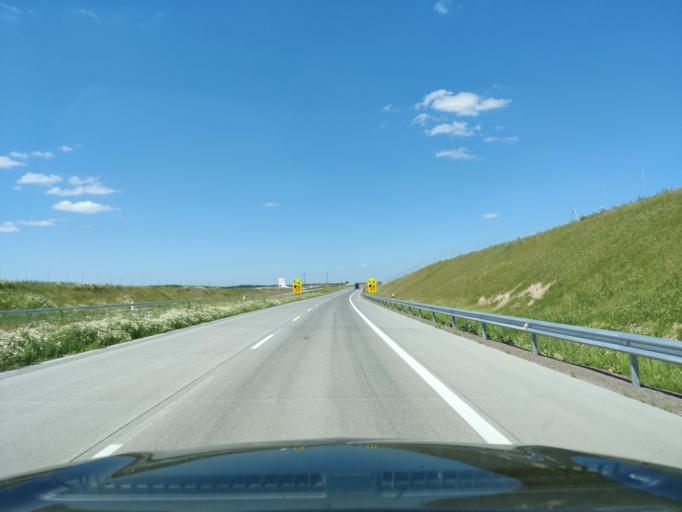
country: PL
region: Masovian Voivodeship
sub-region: Powiat mlawski
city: Mlawa
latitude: 53.1158
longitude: 20.4101
